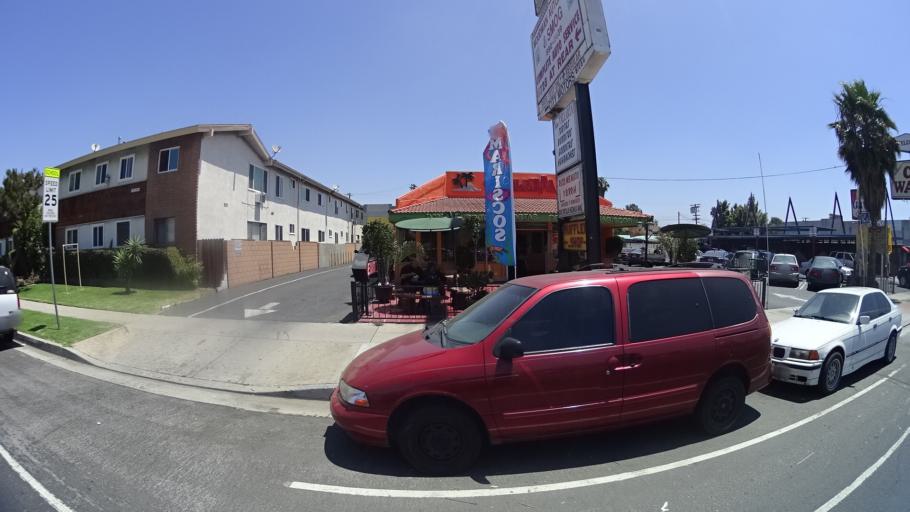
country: US
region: California
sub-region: Los Angeles County
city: Van Nuys
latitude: 34.2287
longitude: -118.4351
